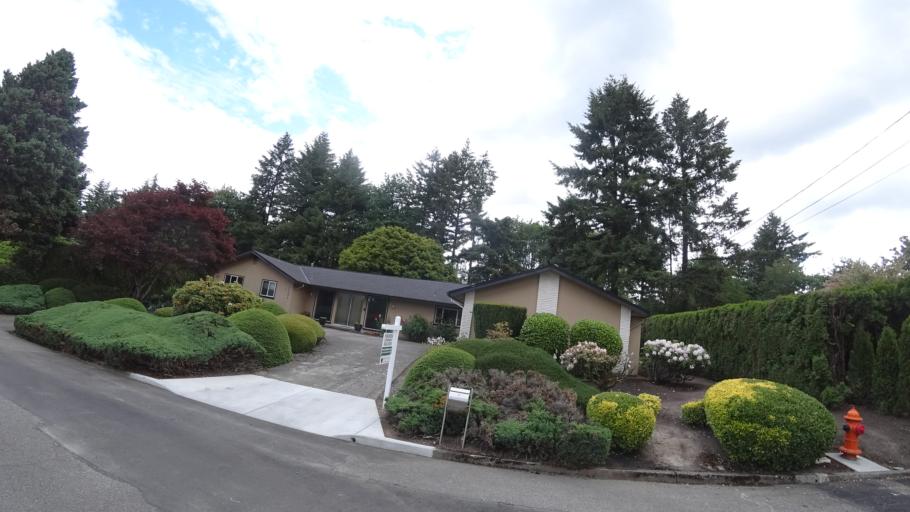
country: US
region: Oregon
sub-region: Clackamas County
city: Lake Oswego
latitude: 45.4486
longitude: -122.6745
